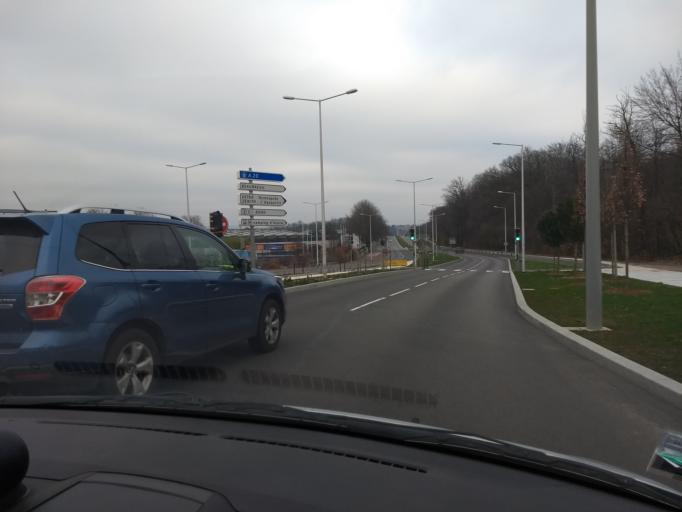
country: FR
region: Limousin
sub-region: Departement de la Haute-Vienne
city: Limoges
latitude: 45.8569
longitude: 1.2698
